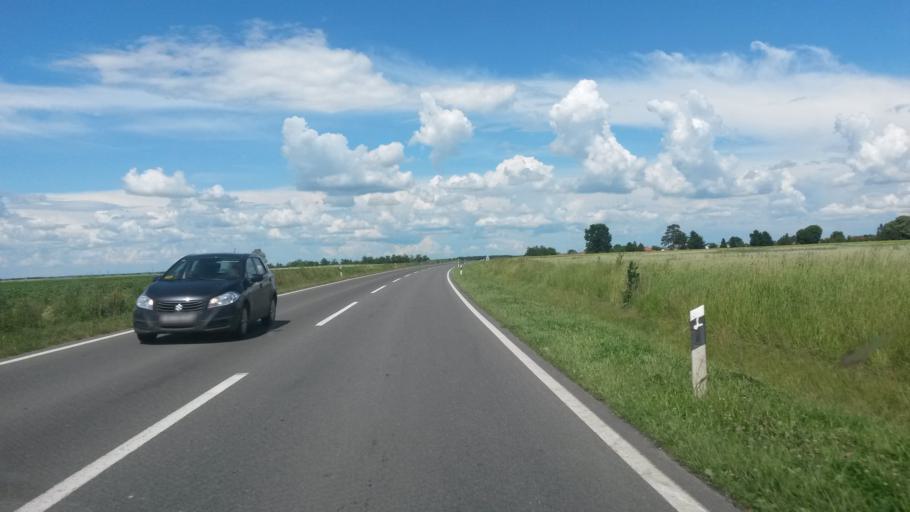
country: HR
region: Osjecko-Baranjska
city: Cepin
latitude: 45.5239
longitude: 18.5395
